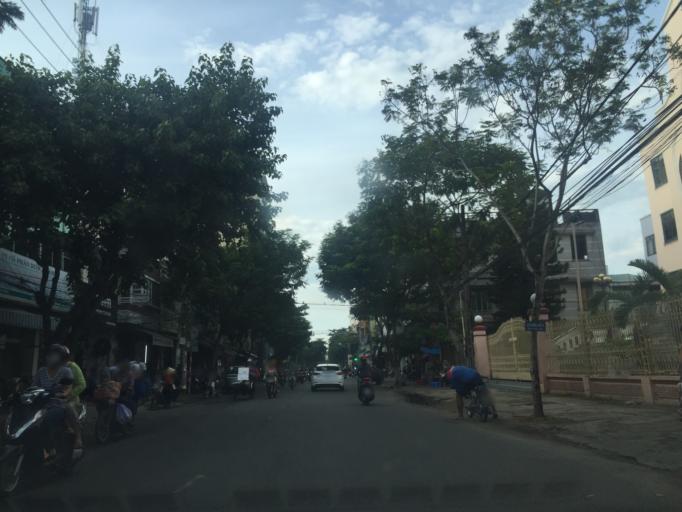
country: VN
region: Da Nang
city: Da Nang
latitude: 16.0713
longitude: 108.2132
